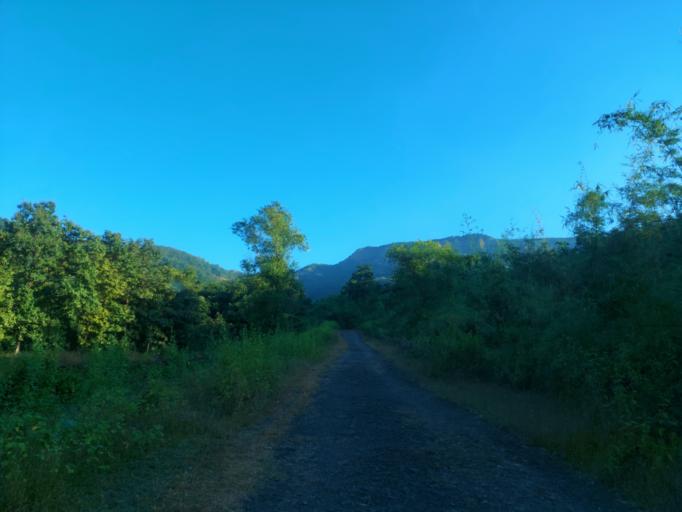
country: IN
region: Maharashtra
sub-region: Sindhudurg
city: Kudal
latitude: 16.0760
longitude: 73.8262
